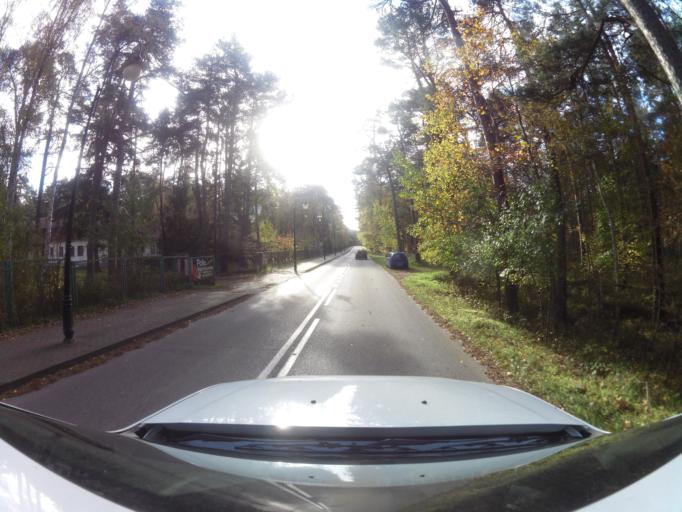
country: PL
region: West Pomeranian Voivodeship
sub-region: Powiat gryficki
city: Cerkwica
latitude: 54.0994
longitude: 15.1213
